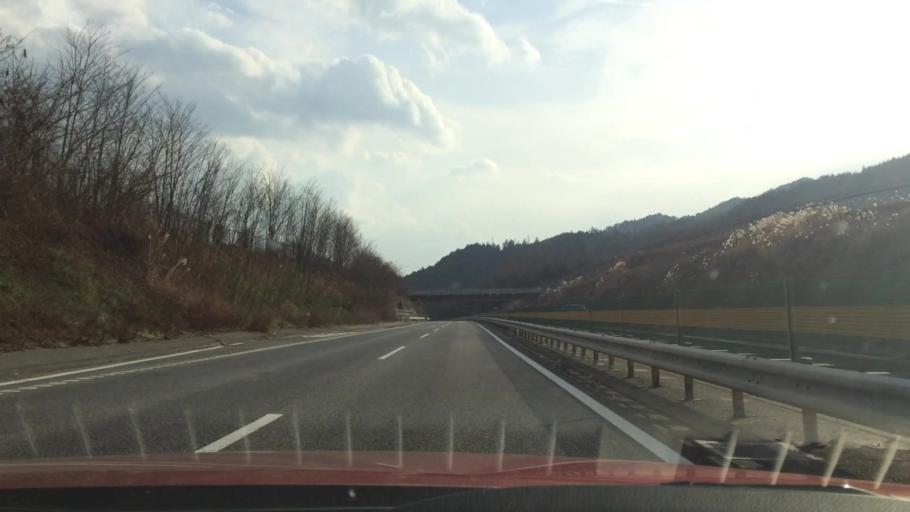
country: JP
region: Nagano
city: Ina
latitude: 35.8038
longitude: 137.9293
